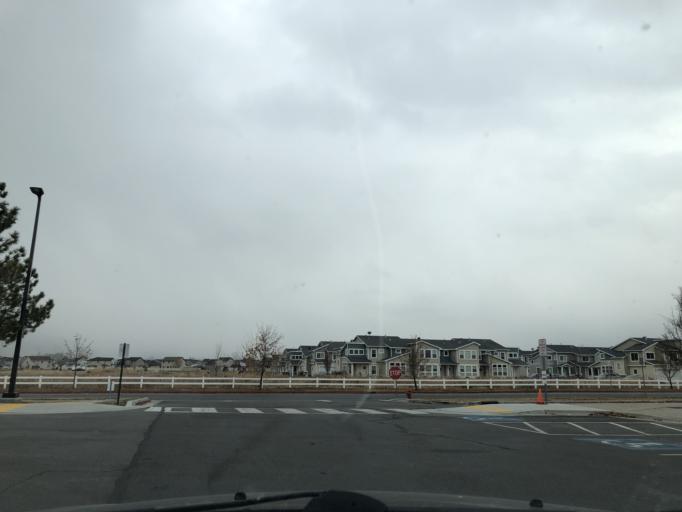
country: US
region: Utah
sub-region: Cache County
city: Nibley
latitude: 41.6907
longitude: -111.8634
